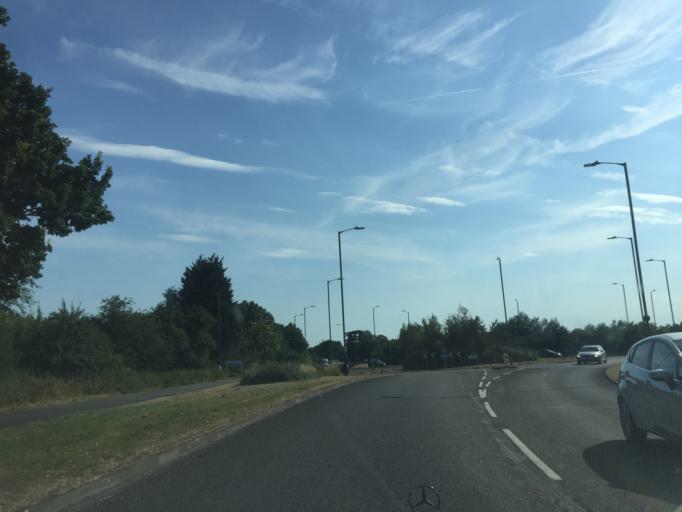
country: GB
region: England
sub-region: Warwickshire
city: Warwick
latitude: 52.2646
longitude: -1.6025
